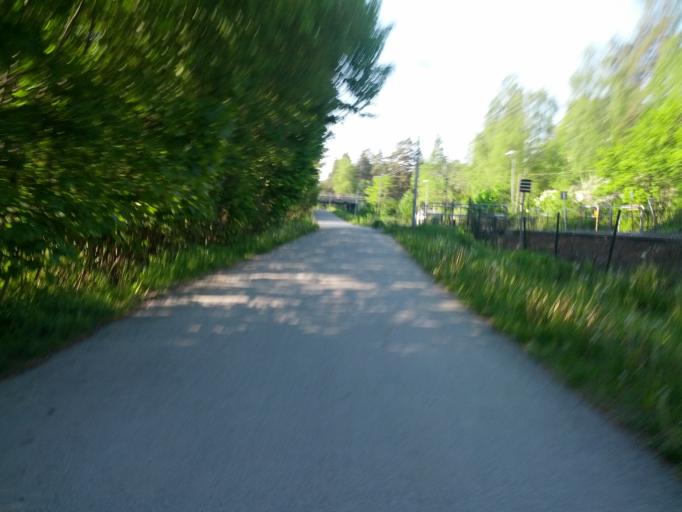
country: SE
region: Stockholm
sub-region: Taby Kommun
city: Taby
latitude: 59.4509
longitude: 18.0634
